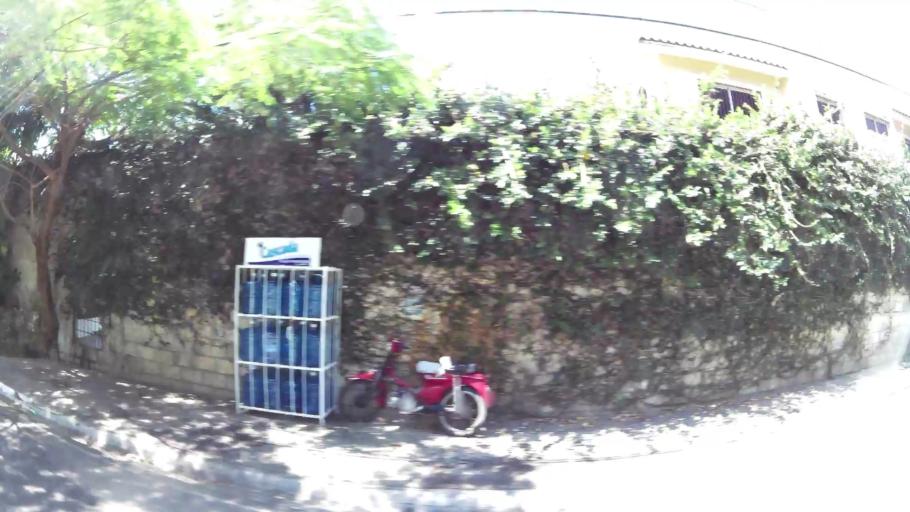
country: DO
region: Santiago
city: Santiago de los Caballeros
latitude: 19.4664
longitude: -70.6754
